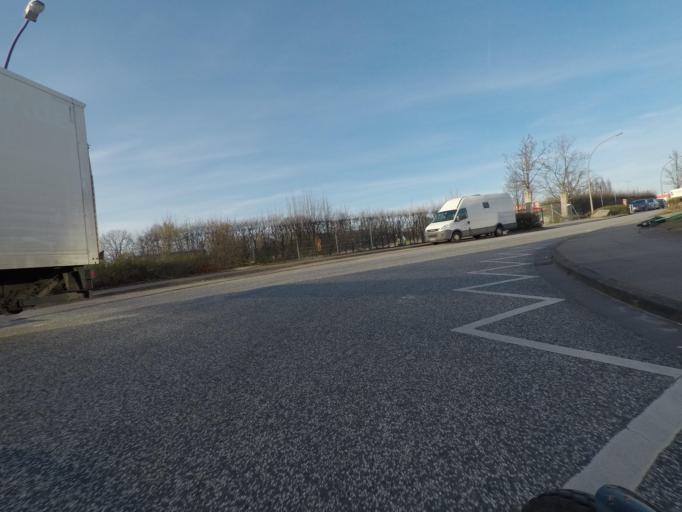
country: DE
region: Hamburg
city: Steilshoop
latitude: 53.6030
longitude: 10.0684
